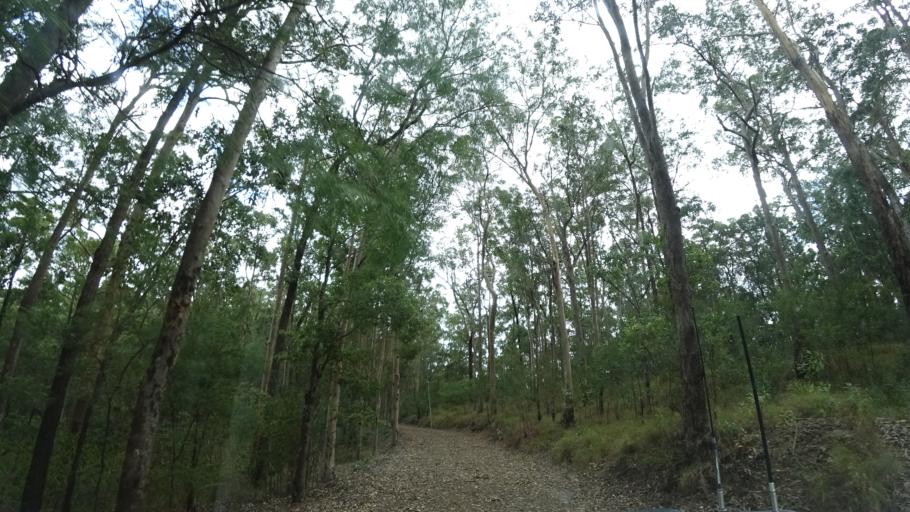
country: AU
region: Queensland
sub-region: Moreton Bay
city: Highvale
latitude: -27.3855
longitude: 152.7557
